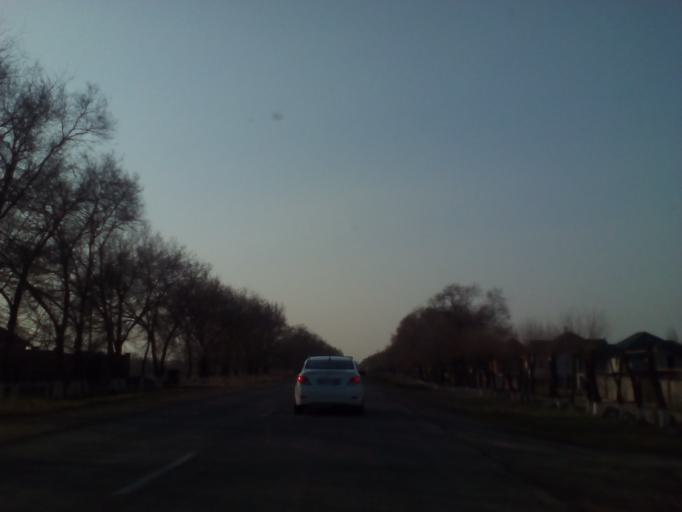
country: KZ
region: Almaty Oblysy
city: Burunday
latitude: 43.1761
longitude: 76.5234
